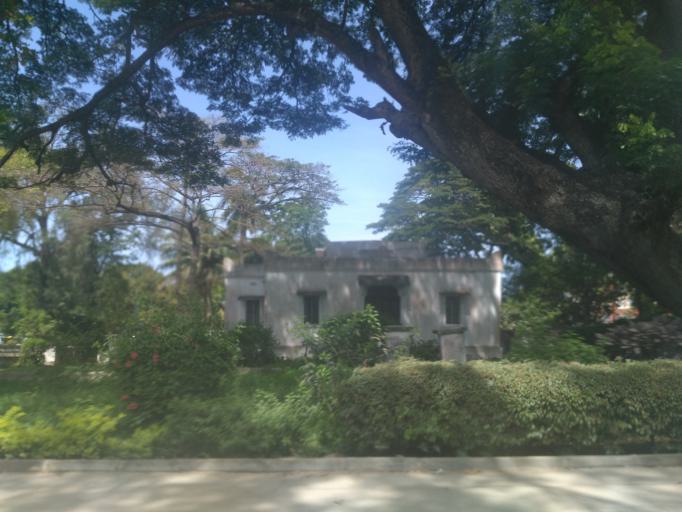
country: TZ
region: Zanzibar Urban/West
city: Zanzibar
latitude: -6.1677
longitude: 39.1918
